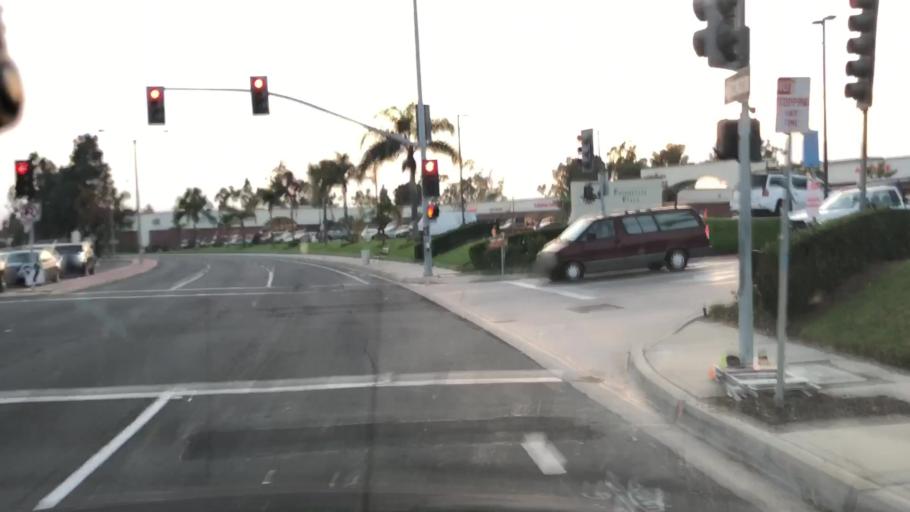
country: US
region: California
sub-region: Ventura County
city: Ventura
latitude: 34.2610
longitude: -119.2340
